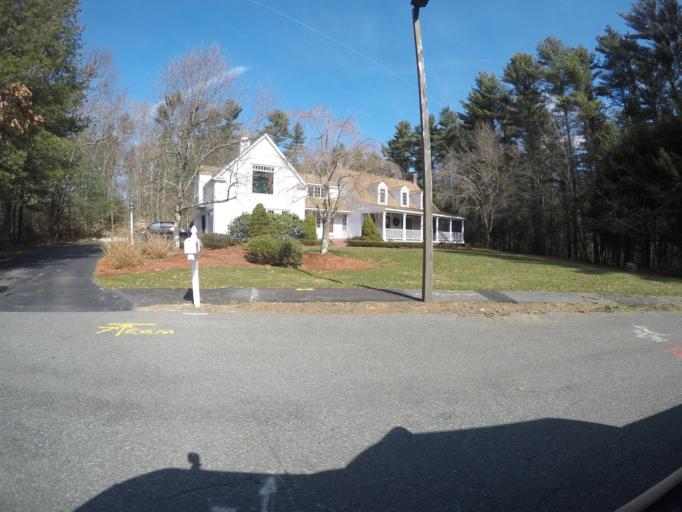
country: US
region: Massachusetts
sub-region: Bristol County
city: Easton
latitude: 42.0160
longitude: -71.1526
